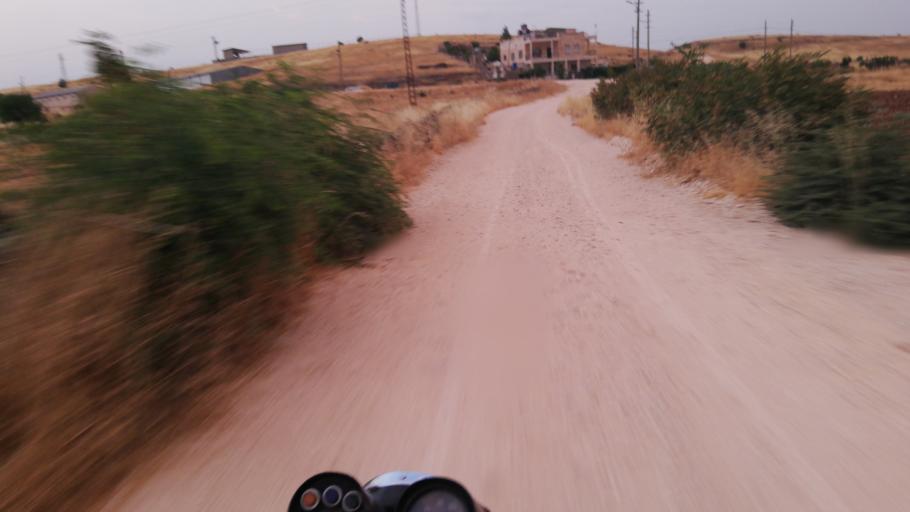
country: TR
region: Mardin
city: Kindirip
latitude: 37.4599
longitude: 41.2211
